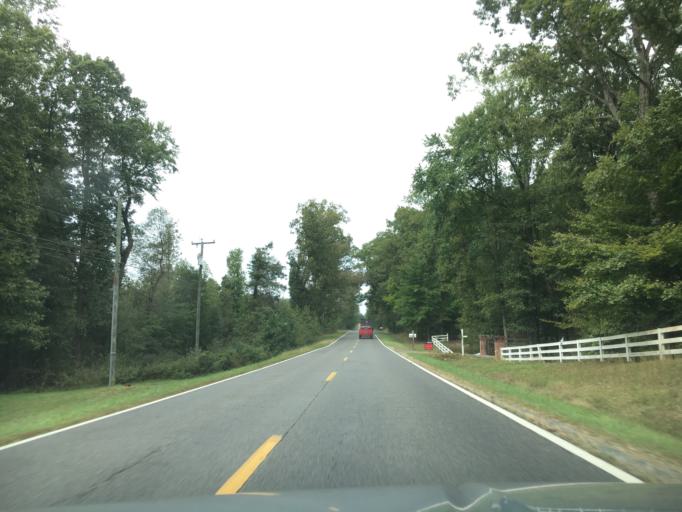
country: US
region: Virginia
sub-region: Goochland County
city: Goochland
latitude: 37.7554
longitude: -77.8670
